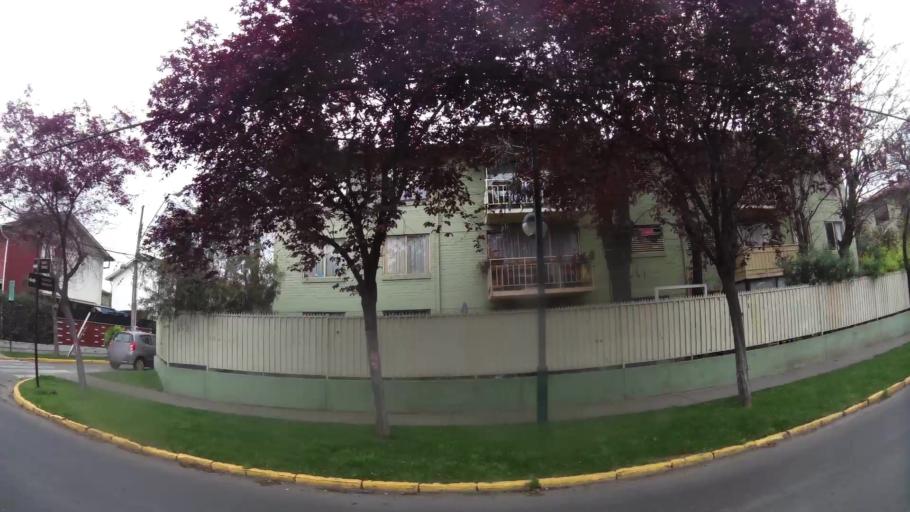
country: CL
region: Santiago Metropolitan
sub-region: Provincia de Santiago
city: Villa Presidente Frei, Nunoa, Santiago, Chile
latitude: -33.4720
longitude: -70.6012
